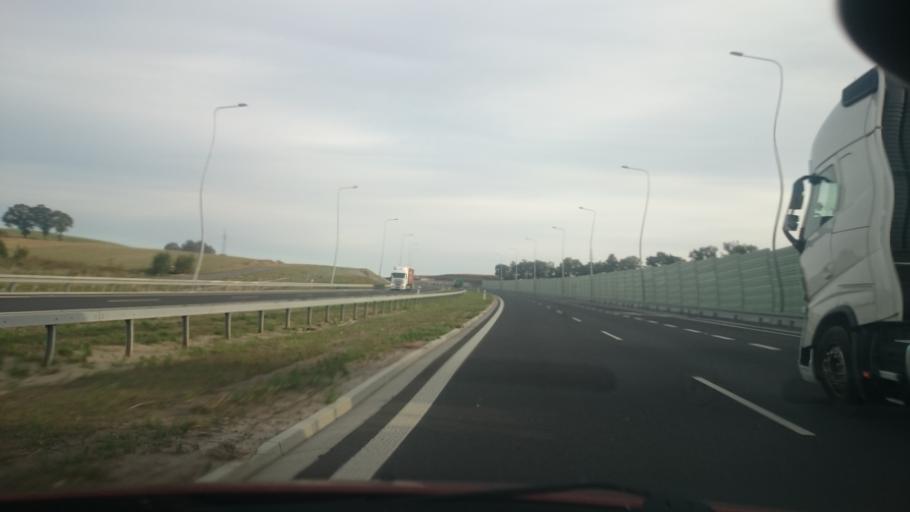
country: PL
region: Lower Silesian Voivodeship
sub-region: Powiat trzebnicki
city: Trzebnica
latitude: 51.2655
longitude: 17.0478
